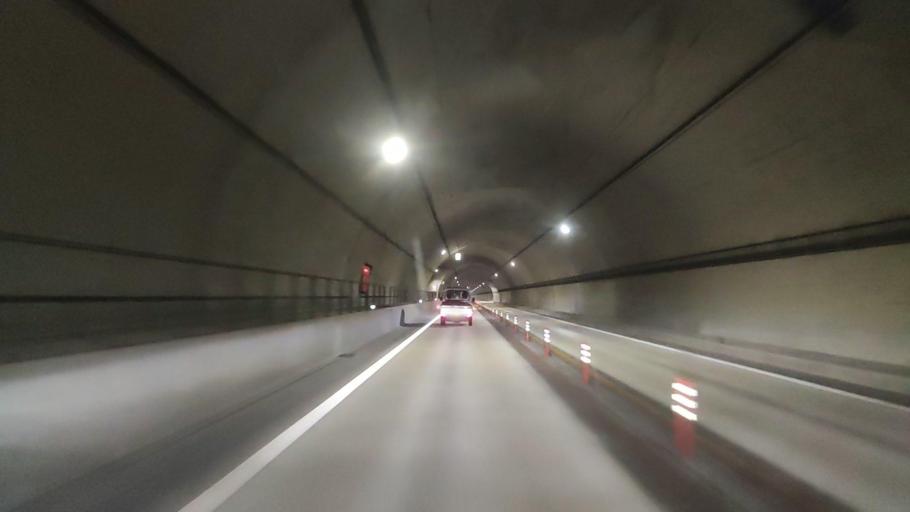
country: JP
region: Wakayama
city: Tanabe
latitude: 33.6213
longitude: 135.4197
